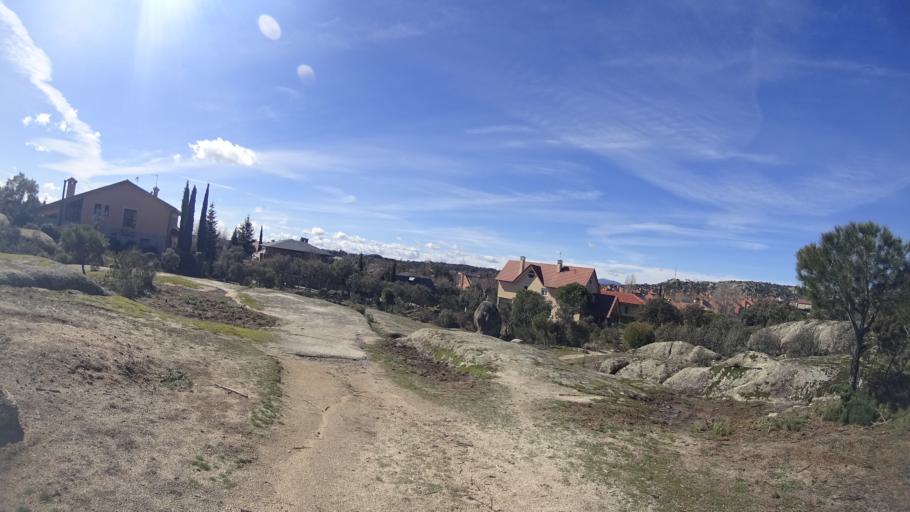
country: ES
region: Madrid
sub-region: Provincia de Madrid
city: Torrelodones
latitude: 40.5816
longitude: -3.9241
